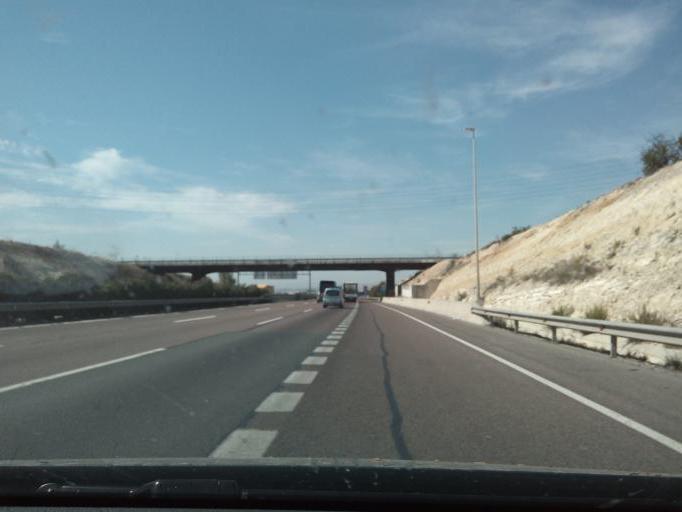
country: ES
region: Valencia
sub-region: Provincia de Valencia
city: Godella
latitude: 39.5367
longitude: -0.4573
